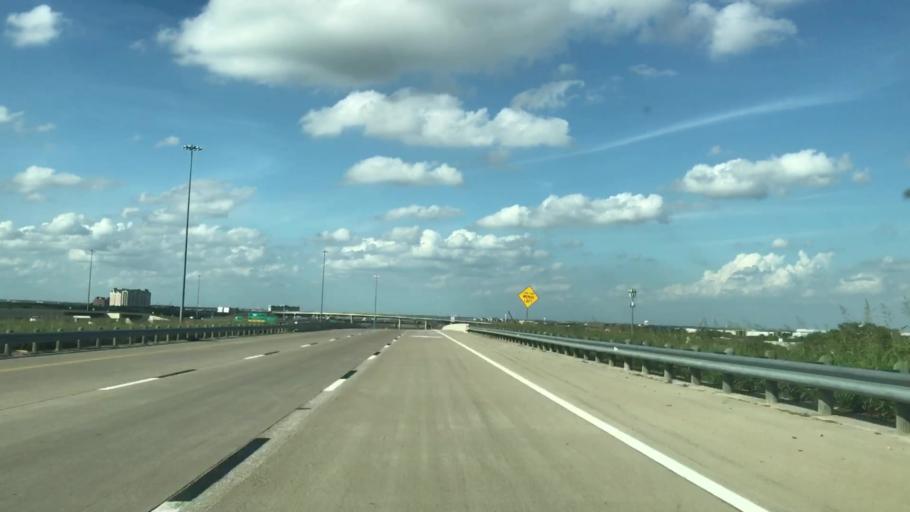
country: US
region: Texas
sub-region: Dallas County
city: Coppell
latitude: 32.9416
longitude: -97.0391
